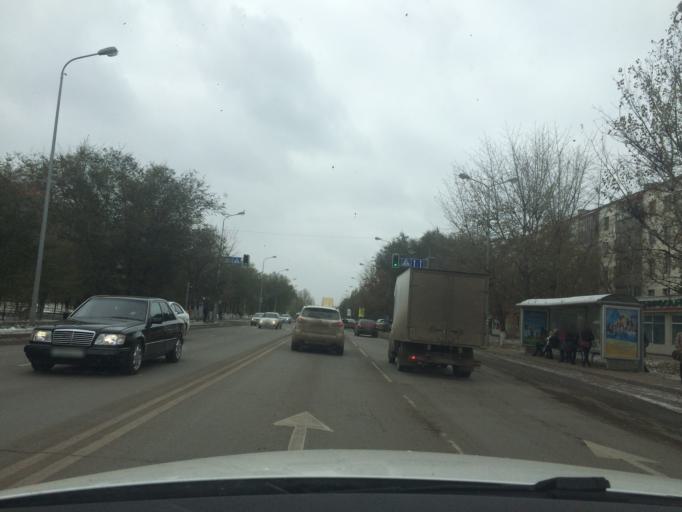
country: KZ
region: Astana Qalasy
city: Astana
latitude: 51.1576
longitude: 71.4600
